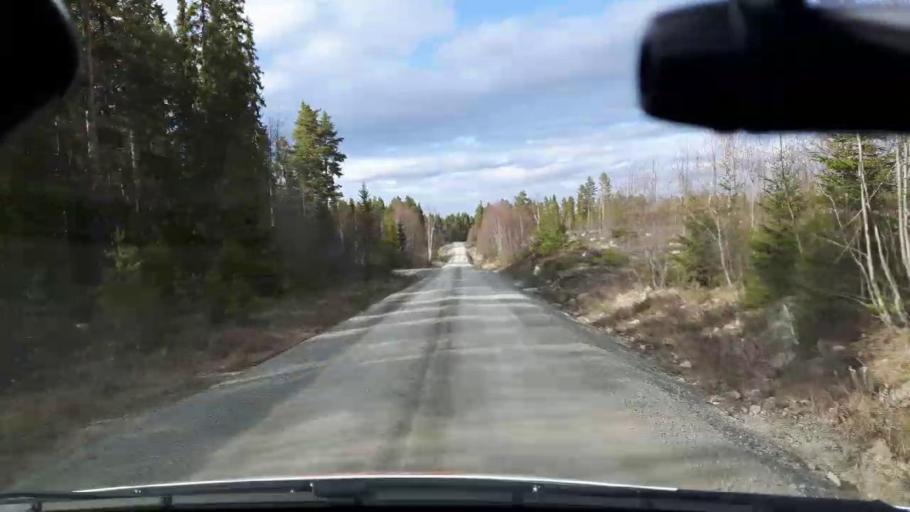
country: SE
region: Jaemtland
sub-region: Bergs Kommun
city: Hoverberg
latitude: 62.9186
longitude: 14.6388
